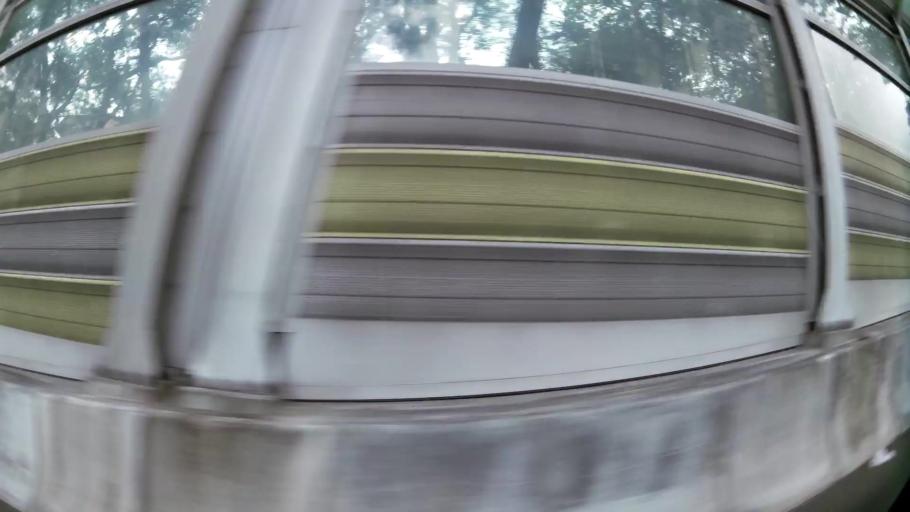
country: HK
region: Tsuen Wan
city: Tsuen Wan
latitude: 22.3772
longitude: 114.1250
